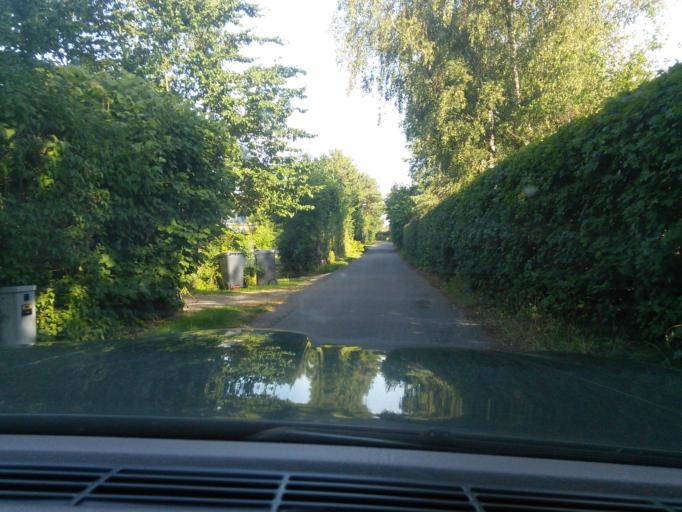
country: DK
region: Capital Region
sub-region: Halsnaes Kommune
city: Liseleje
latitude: 56.0065
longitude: 11.9656
